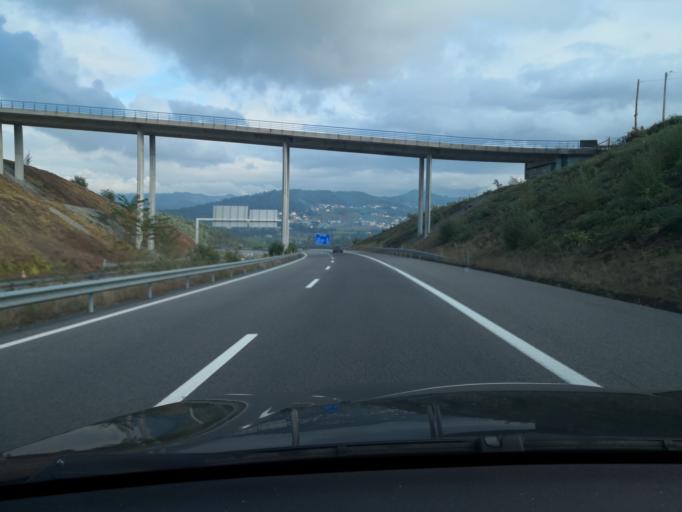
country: PT
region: Braga
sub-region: Guimaraes
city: Serzedo
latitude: 41.3982
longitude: -8.2436
